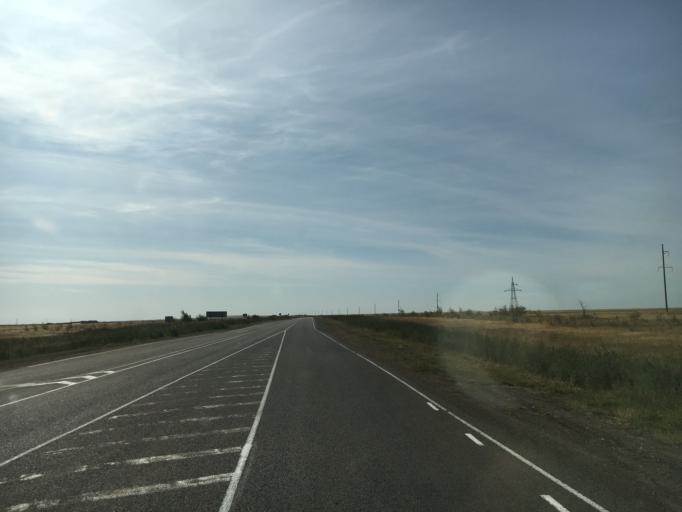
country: KZ
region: Batys Qazaqstan
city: Peremetnoe
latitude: 51.1203
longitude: 50.7381
